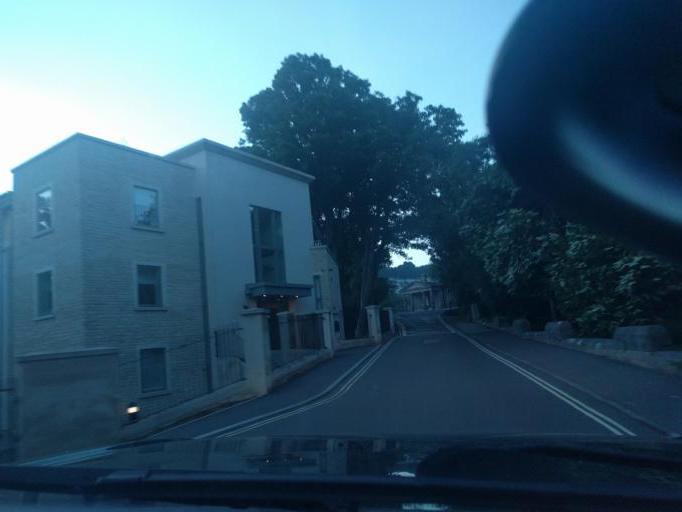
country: GB
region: England
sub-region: Bath and North East Somerset
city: Bath
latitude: 51.3887
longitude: -2.3559
